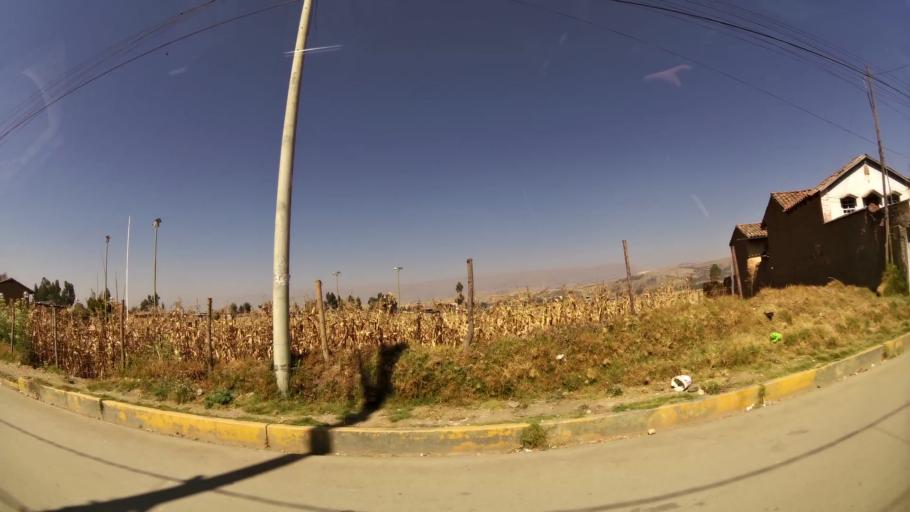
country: PE
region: Junin
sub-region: Provincia de Huancayo
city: San Jeronimo
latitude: -11.9431
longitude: -75.2919
